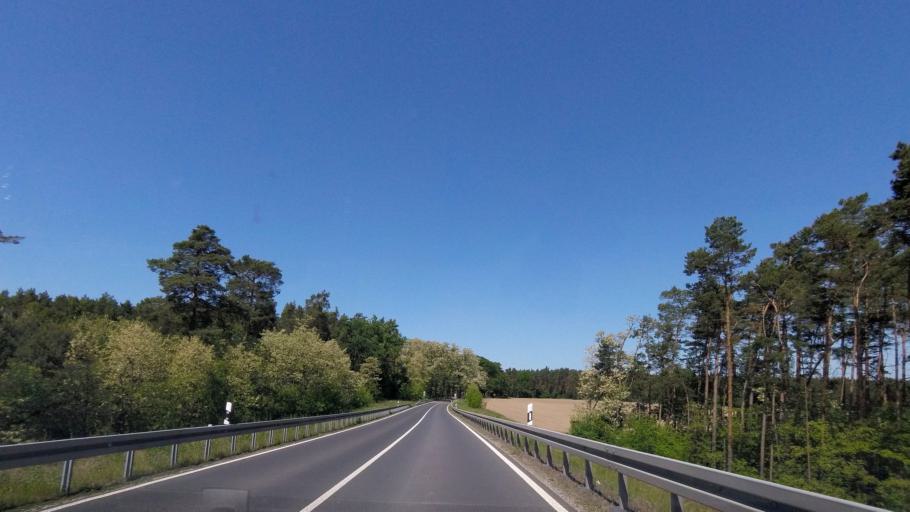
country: DE
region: Brandenburg
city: Trebbin
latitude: 52.2607
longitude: 13.2306
